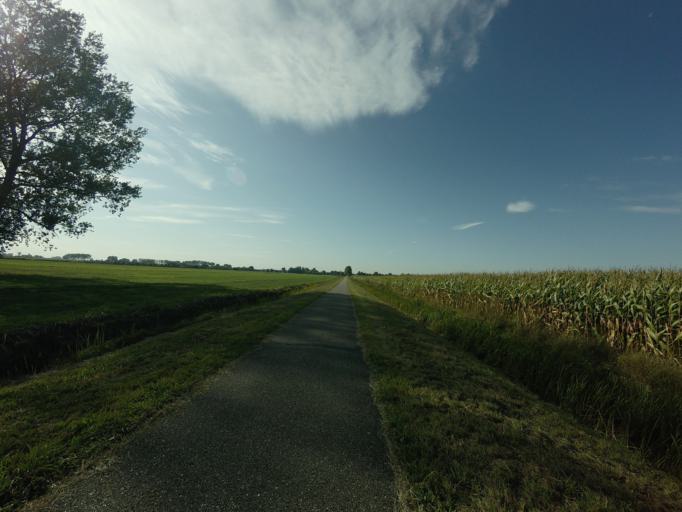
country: NL
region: South Holland
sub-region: Gemeente Leerdam
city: Leerdam
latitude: 51.9273
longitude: 5.0763
